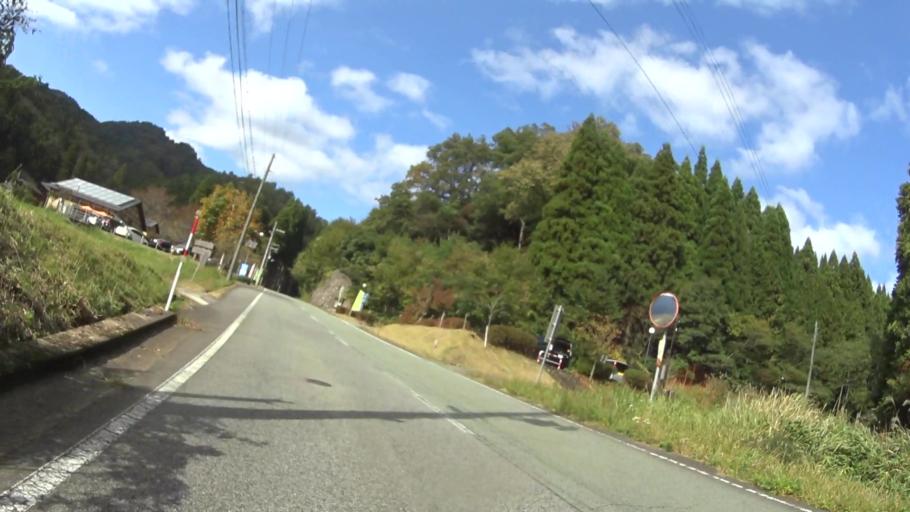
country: JP
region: Hyogo
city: Toyooka
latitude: 35.5130
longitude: 134.9915
